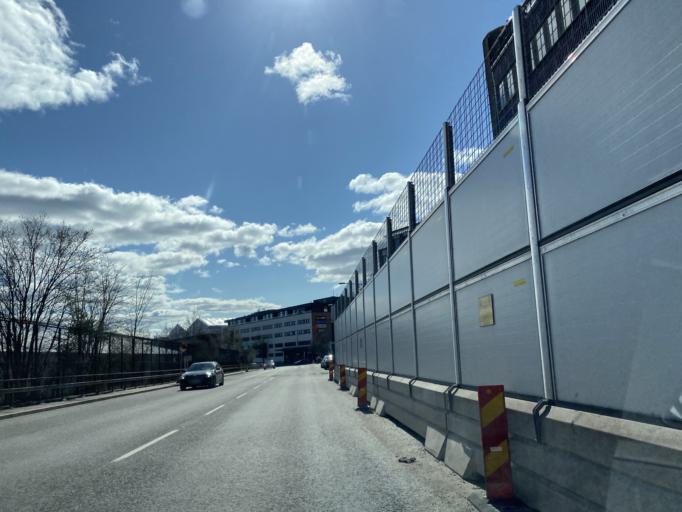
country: SE
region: Stockholm
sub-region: Stockholms Kommun
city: OEstermalm
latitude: 59.3435
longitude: 18.1141
